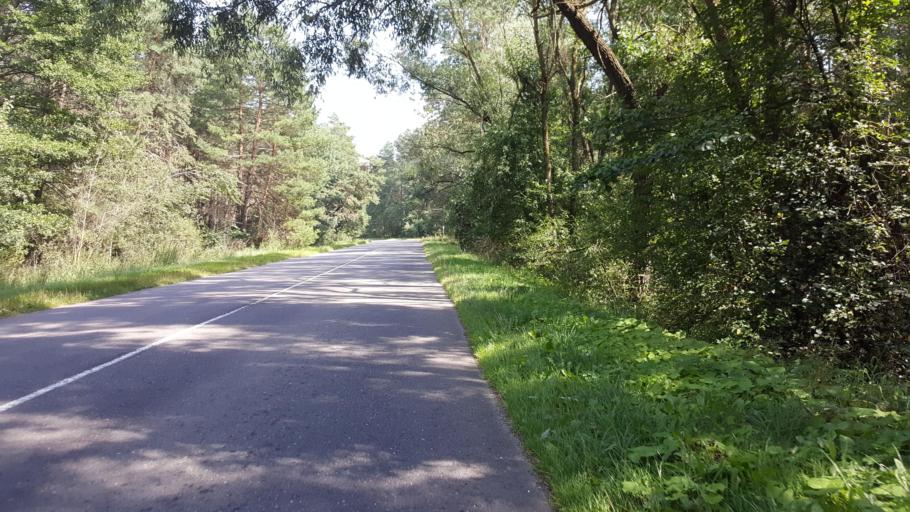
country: BY
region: Brest
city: Kamyanyuki
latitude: 52.5048
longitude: 23.6415
